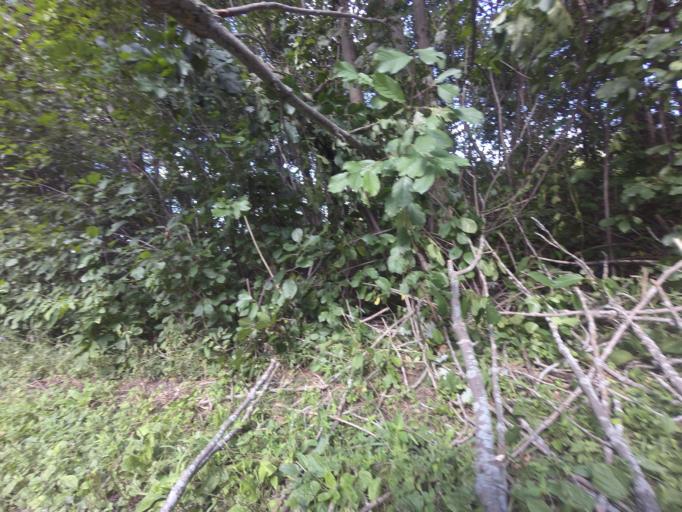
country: CA
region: Ontario
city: Huron East
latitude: 43.6774
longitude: -81.2925
